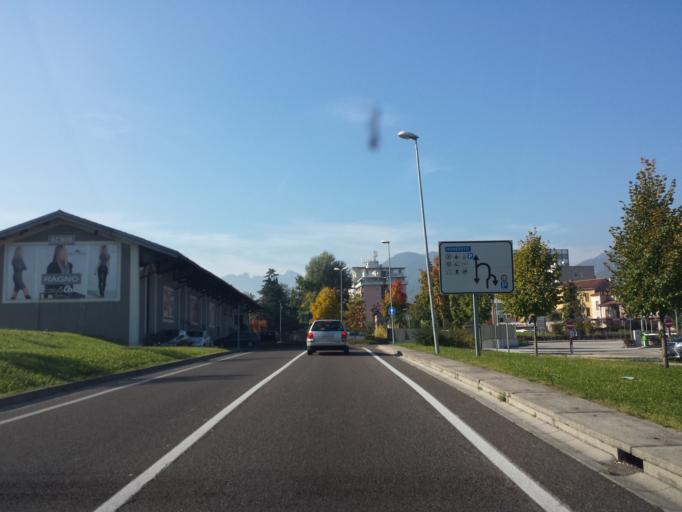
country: IT
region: Veneto
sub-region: Provincia di Vicenza
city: Schio
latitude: 45.7101
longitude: 11.3604
